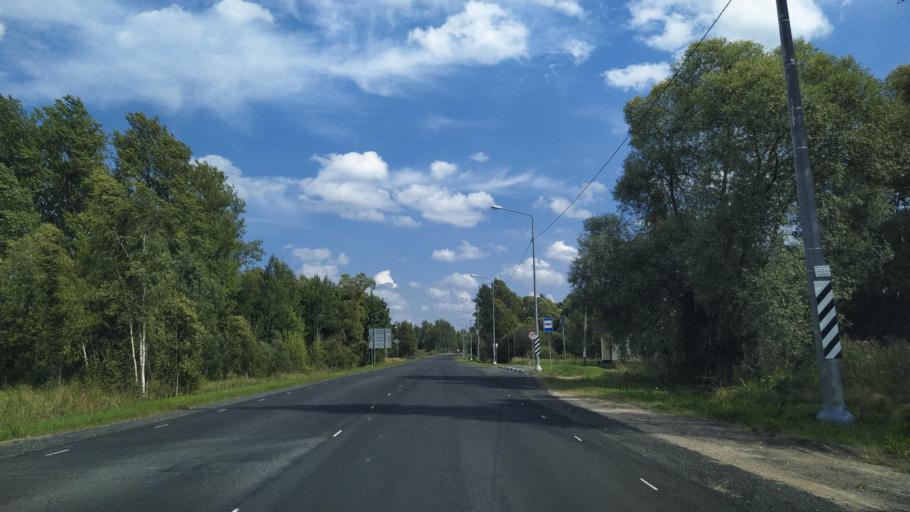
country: RU
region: Pskov
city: Porkhov
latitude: 57.7277
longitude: 29.1590
